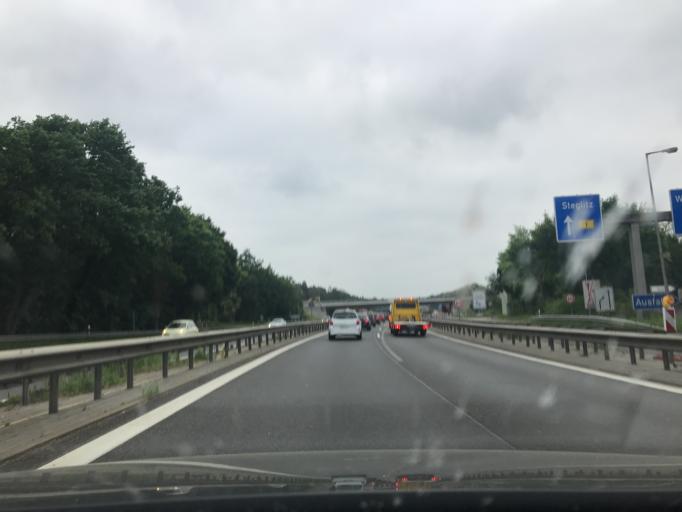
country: DE
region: Berlin
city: Nikolassee
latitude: 52.4232
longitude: 13.1952
